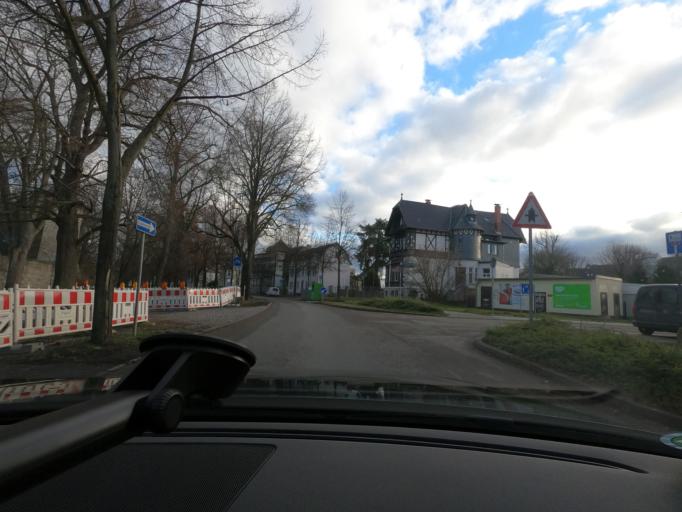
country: DE
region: Thuringia
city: Muehlhausen
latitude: 51.2064
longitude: 10.4548
